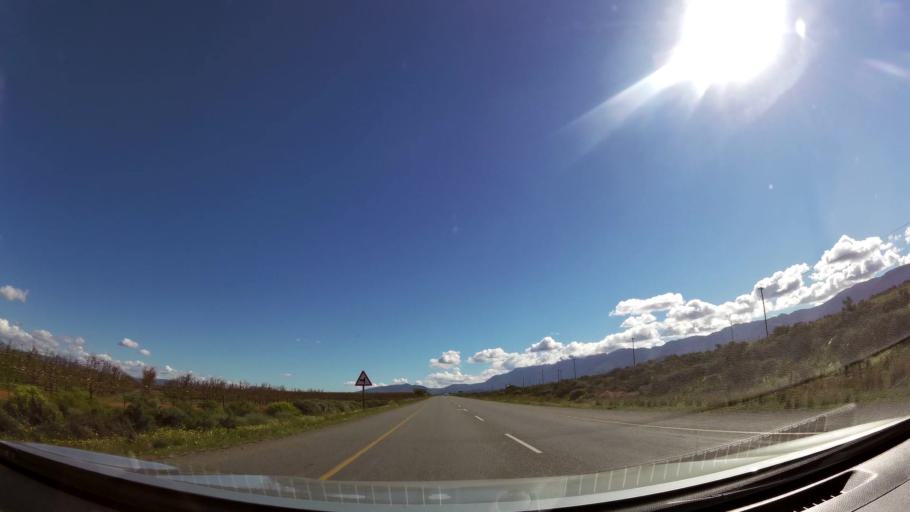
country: ZA
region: Western Cape
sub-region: Cape Winelands District Municipality
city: Ashton
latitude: -33.8382
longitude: 20.0078
